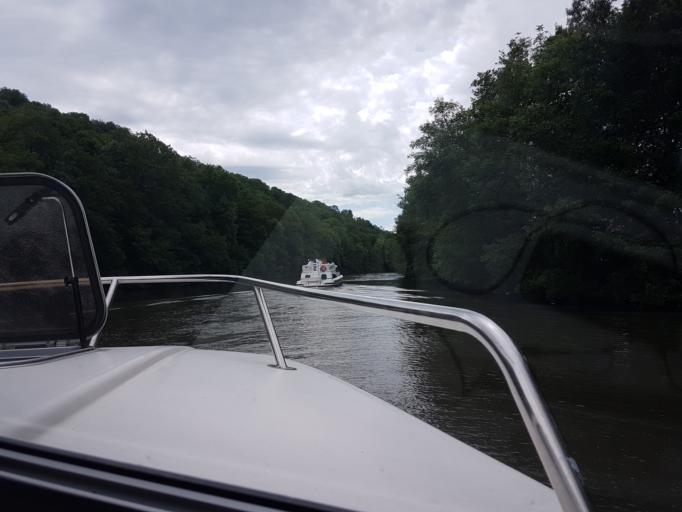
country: FR
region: Bourgogne
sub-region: Departement de la Nievre
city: Clamecy
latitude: 47.4683
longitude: 3.5283
